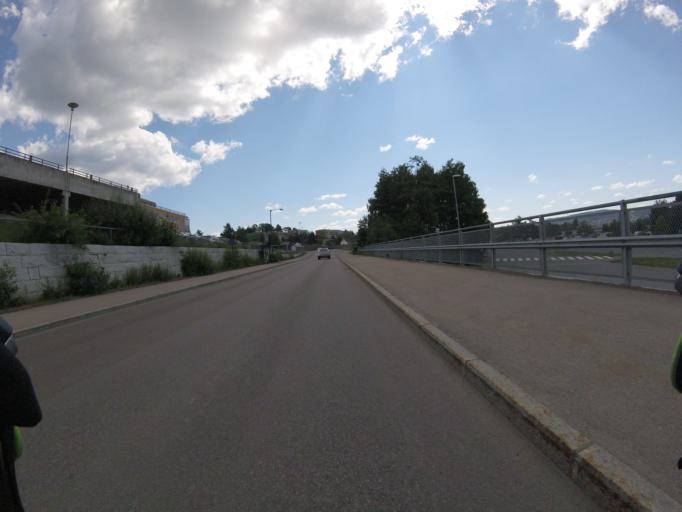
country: NO
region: Akershus
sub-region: Skedsmo
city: Lillestrom
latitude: 59.9715
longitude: 11.0506
